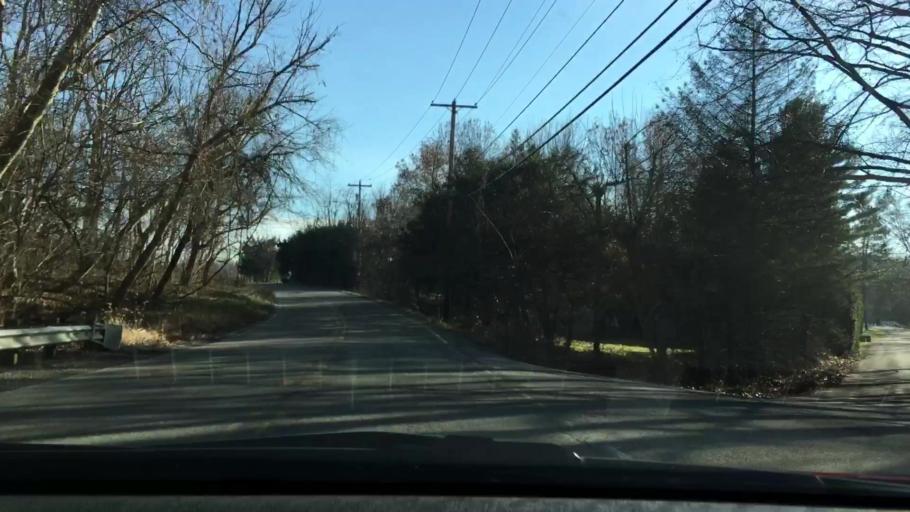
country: US
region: Pennsylvania
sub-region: Westmoreland County
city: Irwin
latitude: 40.2650
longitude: -79.6978
